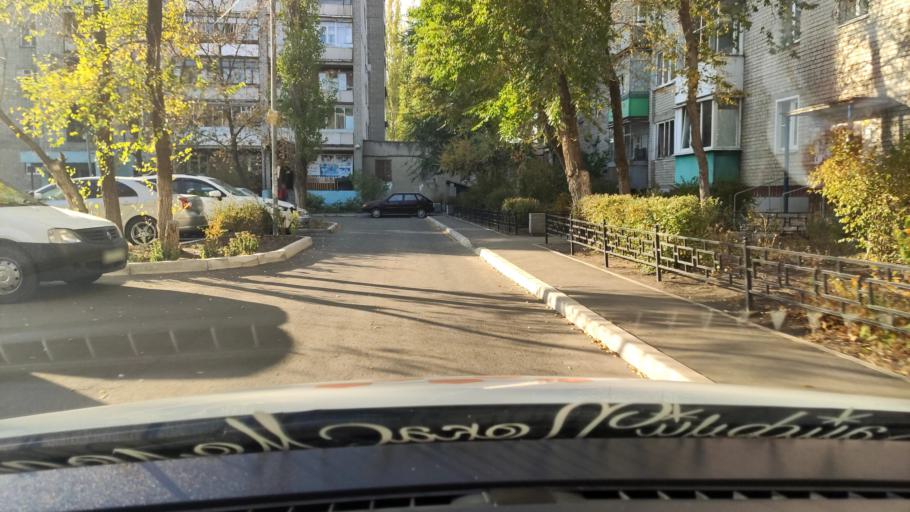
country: RU
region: Voronezj
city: Voronezh
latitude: 51.6933
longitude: 39.2562
